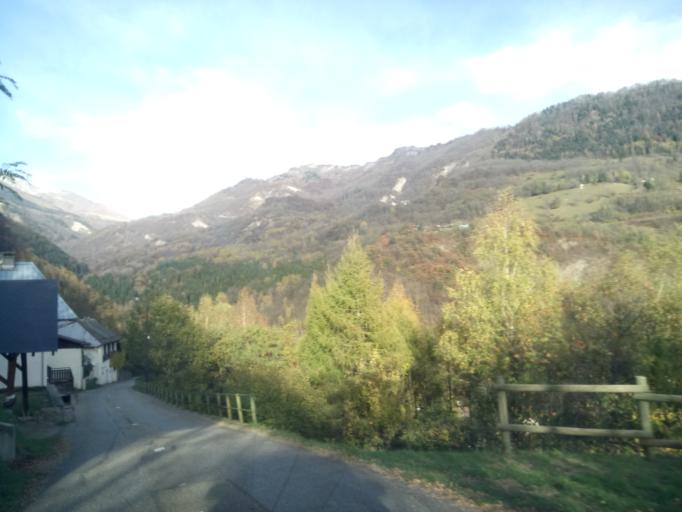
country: FR
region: Rhone-Alpes
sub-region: Departement de la Savoie
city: La Chambre
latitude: 45.3737
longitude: 6.3115
